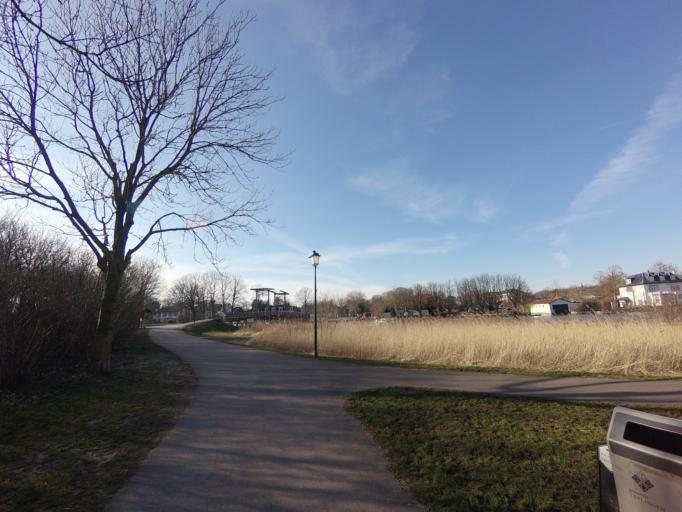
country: NL
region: South Holland
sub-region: Gemeente Teylingen
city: Voorhout
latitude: 52.1940
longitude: 4.5046
